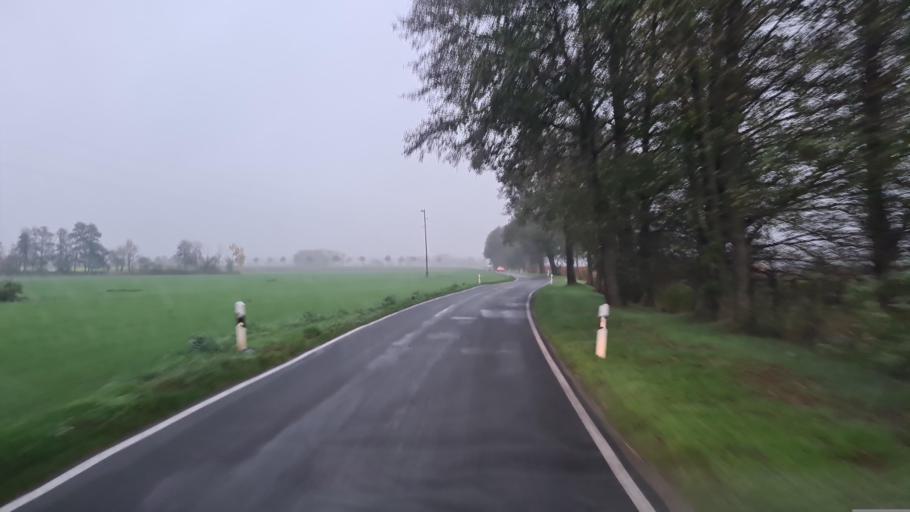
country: DE
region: Brandenburg
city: Beelitz
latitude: 52.2361
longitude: 13.0093
